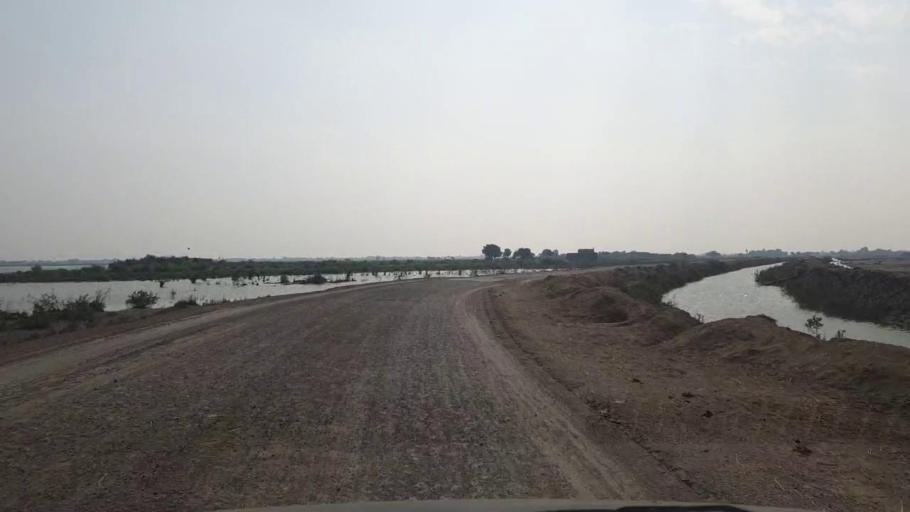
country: PK
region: Sindh
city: Tando Muhammad Khan
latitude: 25.0839
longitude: 68.3877
